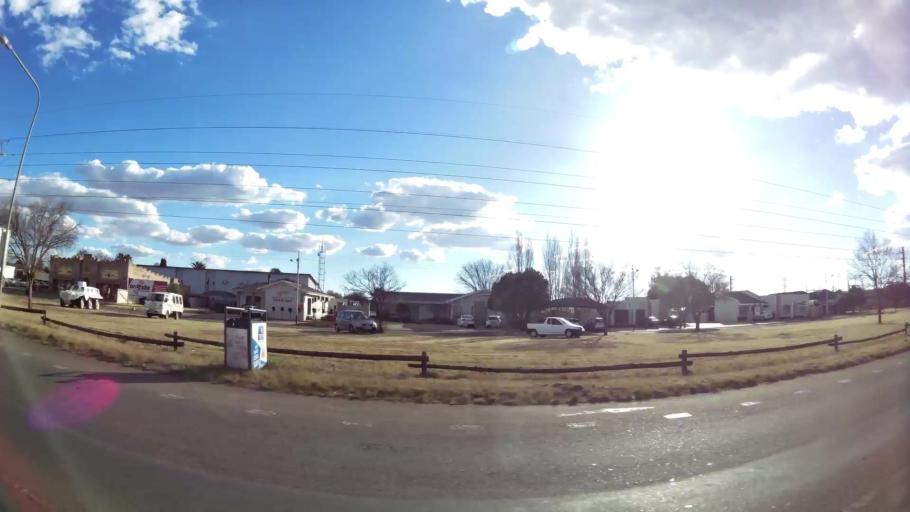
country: ZA
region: North-West
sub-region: Dr Kenneth Kaunda District Municipality
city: Potchefstroom
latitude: -26.7031
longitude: 27.1041
